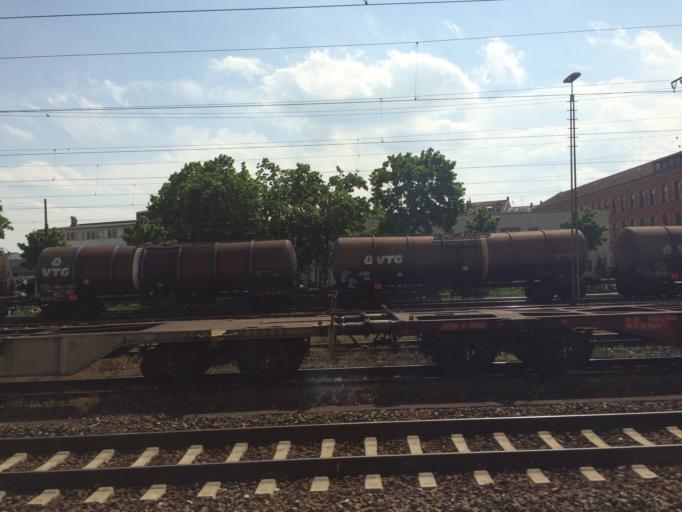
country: DE
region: Bavaria
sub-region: Regierungsbezirk Mittelfranken
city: Furth
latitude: 49.4665
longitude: 11.0045
